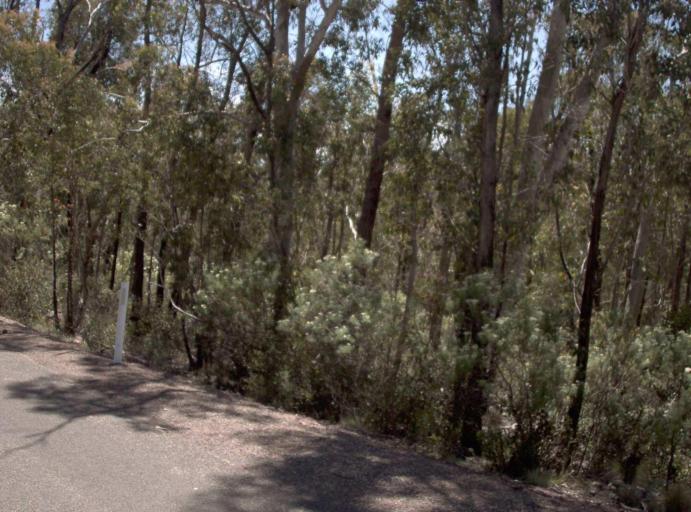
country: AU
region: New South Wales
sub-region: Snowy River
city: Jindabyne
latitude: -37.1098
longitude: 148.2516
